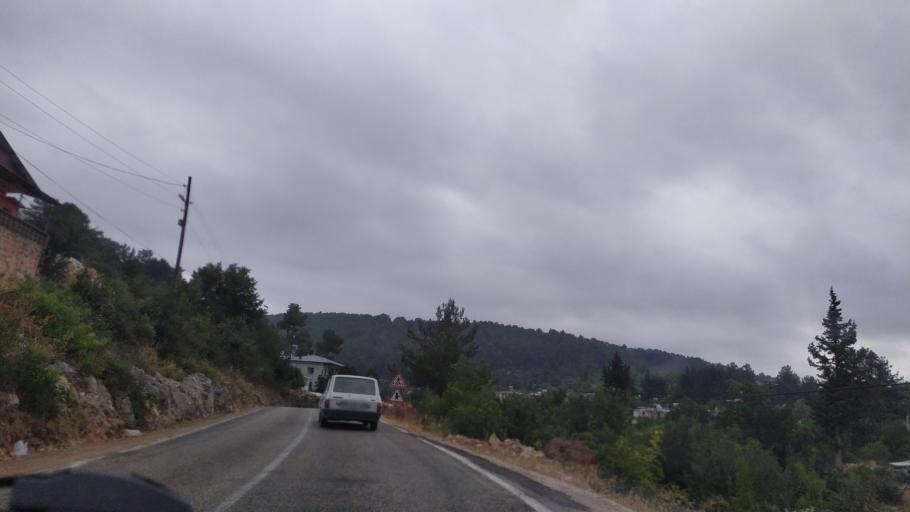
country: TR
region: Mersin
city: Silifke
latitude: 36.5361
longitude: 33.9422
